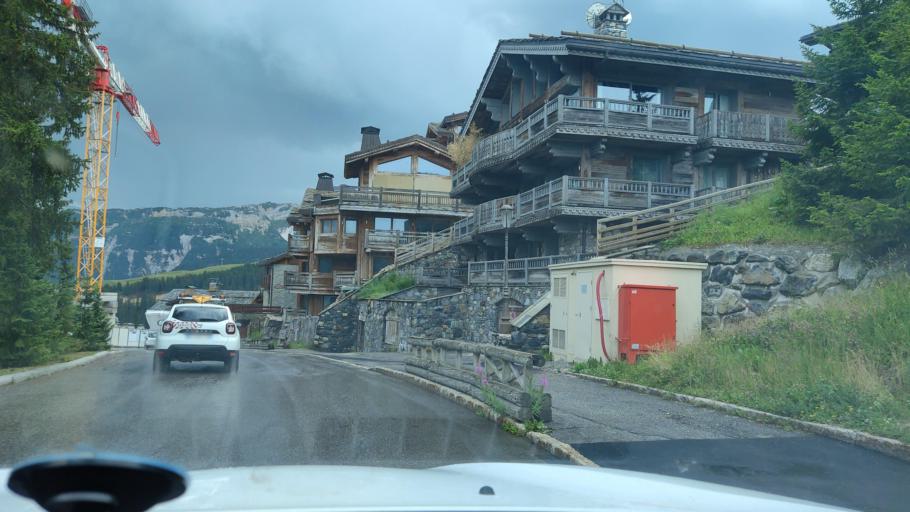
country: FR
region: Rhone-Alpes
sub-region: Departement de la Savoie
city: Courchevel
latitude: 45.4128
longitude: 6.6369
